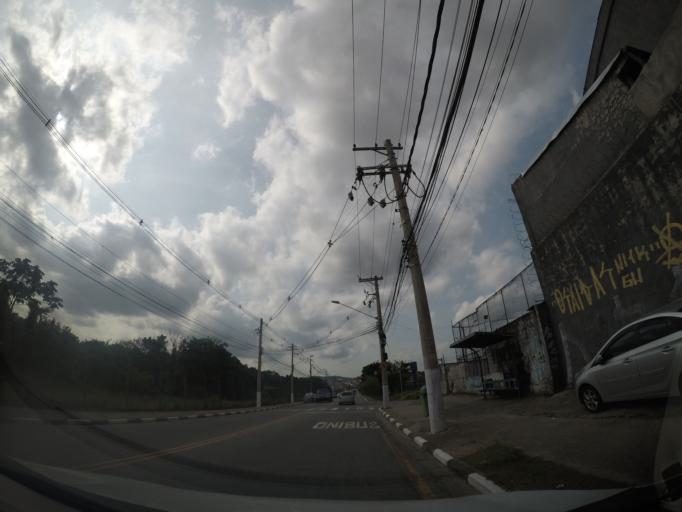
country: BR
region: Sao Paulo
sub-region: Guarulhos
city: Guarulhos
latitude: -23.4204
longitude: -46.4420
